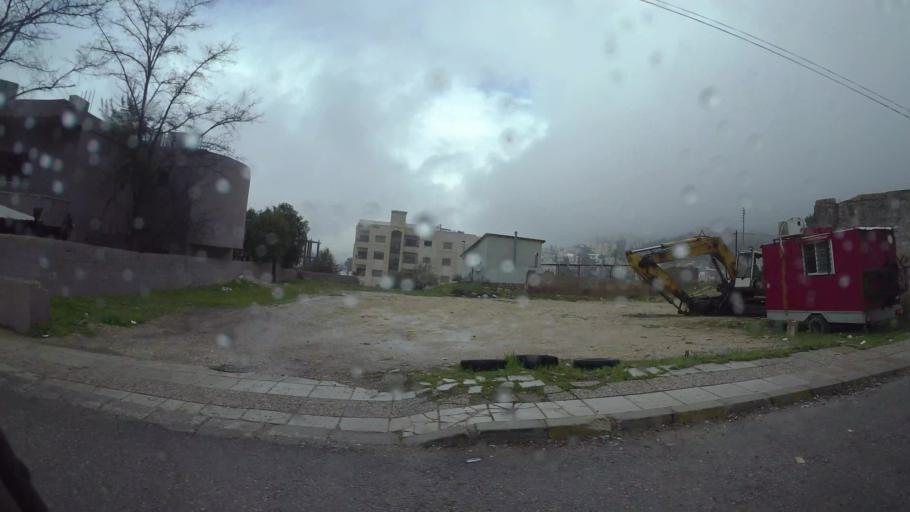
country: JO
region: Amman
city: Wadi as Sir
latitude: 32.0031
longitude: 35.7856
